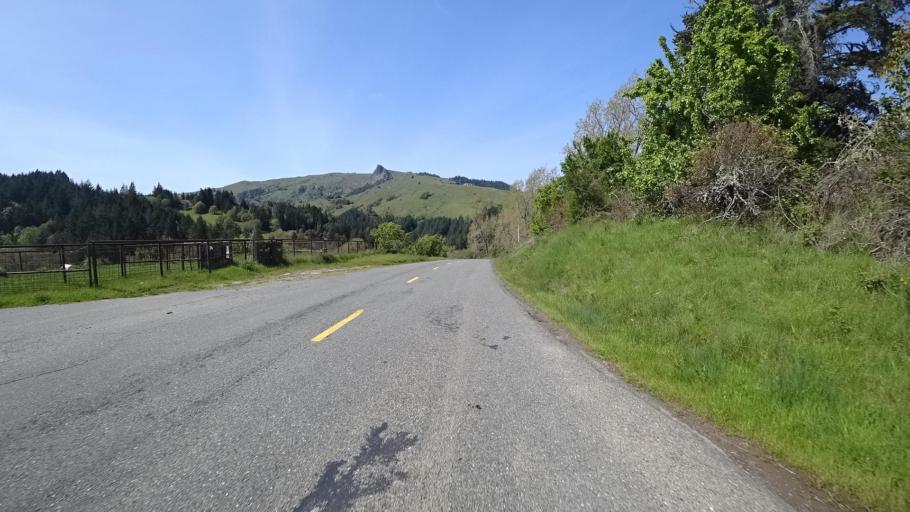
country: US
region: California
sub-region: Humboldt County
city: Rio Dell
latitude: 40.4603
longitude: -123.8045
